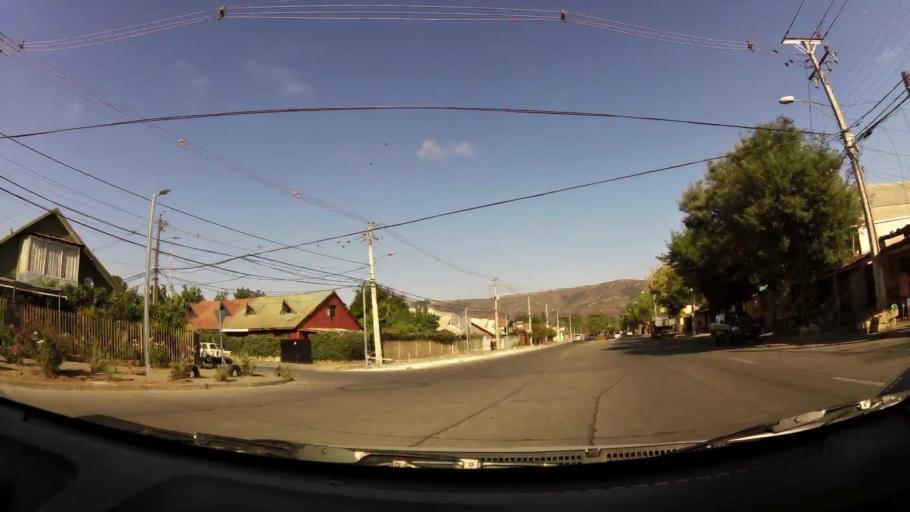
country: CL
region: Maule
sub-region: Provincia de Talca
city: Talca
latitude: -35.4102
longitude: -71.6631
